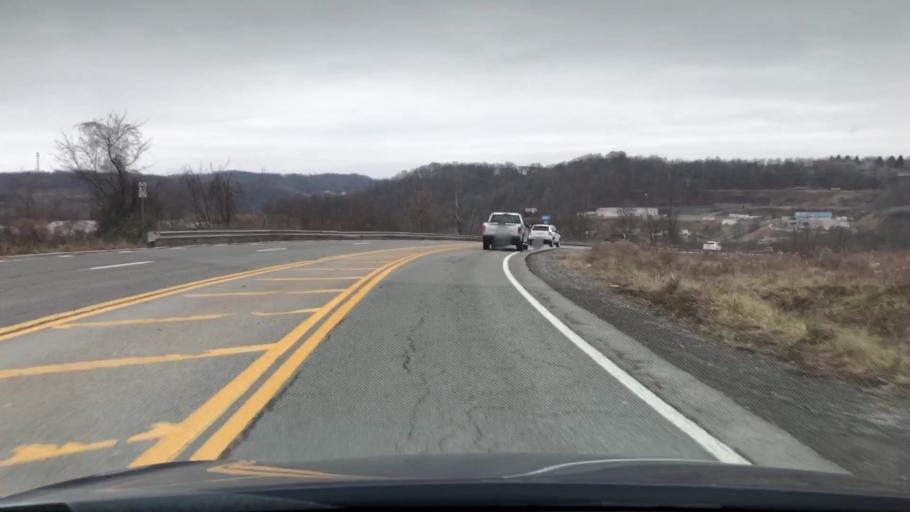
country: US
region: West Virginia
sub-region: Monongalia County
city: Morgantown
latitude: 39.5799
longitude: -79.9542
